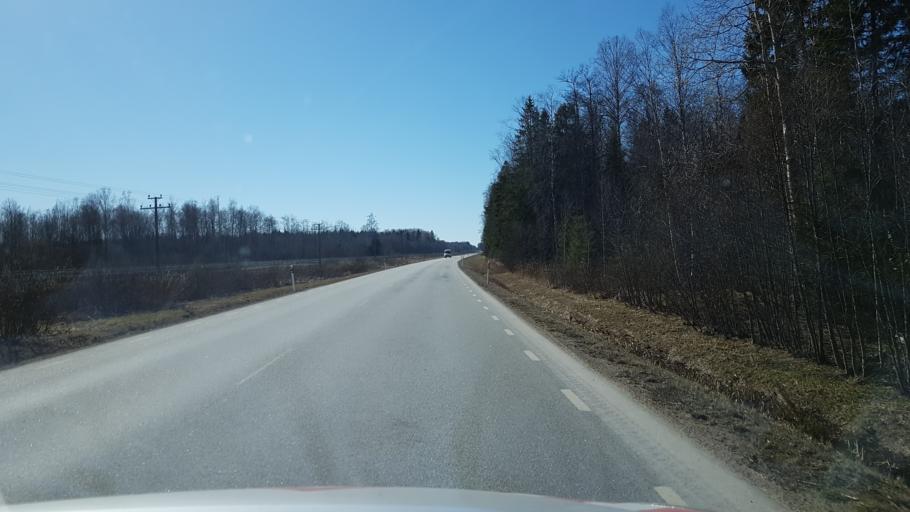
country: EE
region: Ida-Virumaa
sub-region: Aseri vald
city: Aseri
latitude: 59.3487
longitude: 26.8053
